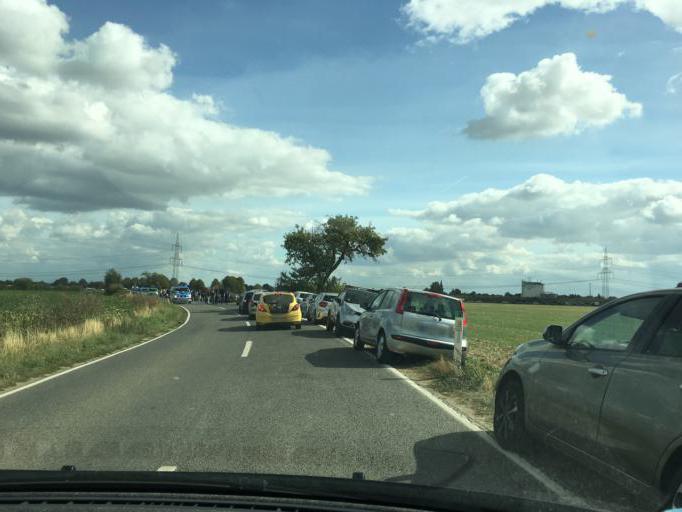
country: DE
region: North Rhine-Westphalia
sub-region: Regierungsbezirk Koln
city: Merzenich
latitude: 50.8680
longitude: 6.5647
